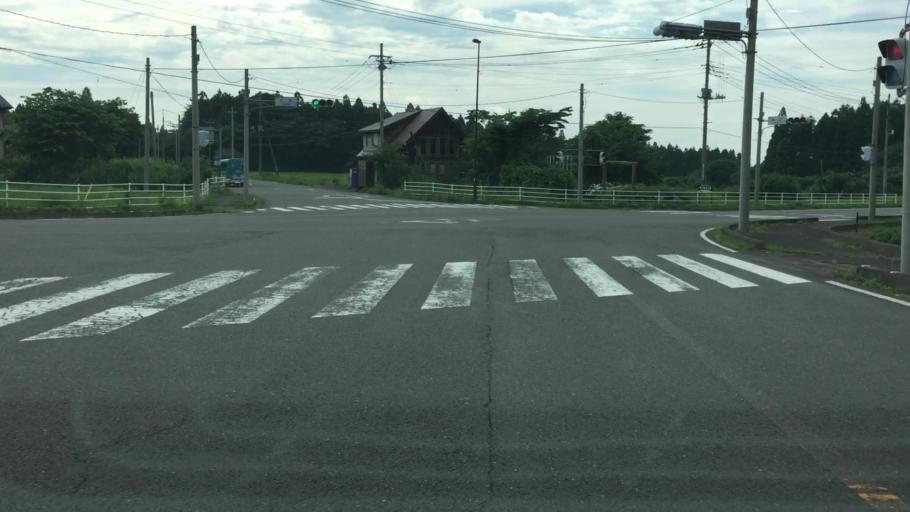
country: JP
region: Tochigi
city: Kuroiso
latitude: 37.0917
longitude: 140.0607
